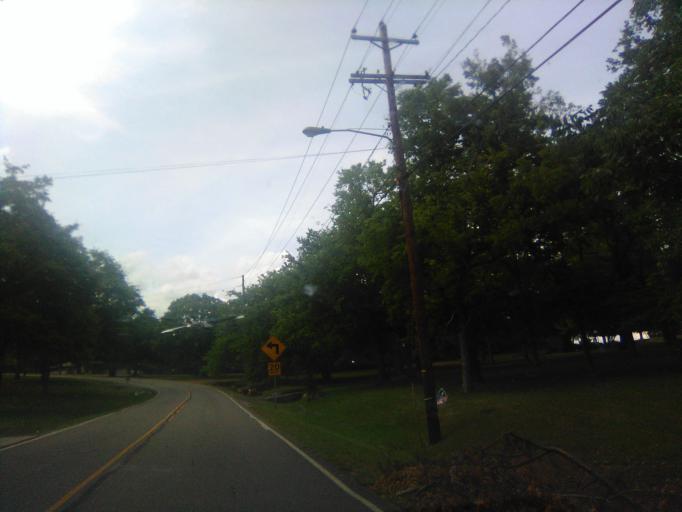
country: US
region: Tennessee
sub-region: Davidson County
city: Belle Meade
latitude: 36.0944
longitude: -86.8867
